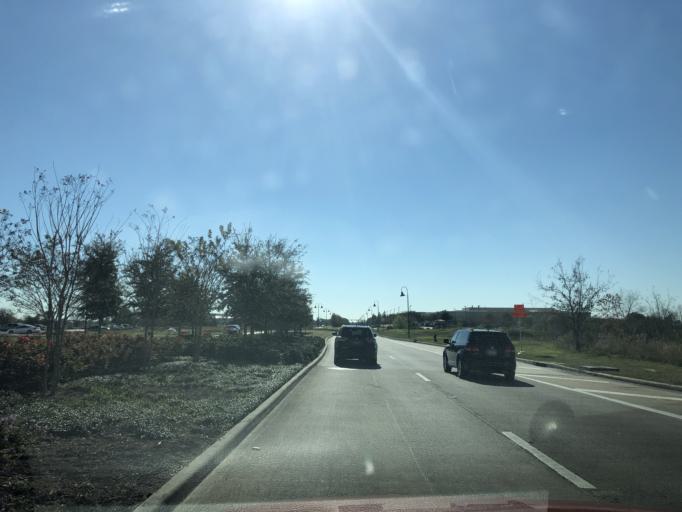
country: US
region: Texas
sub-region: Fort Bend County
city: Fresno
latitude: 29.5964
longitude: -95.4007
